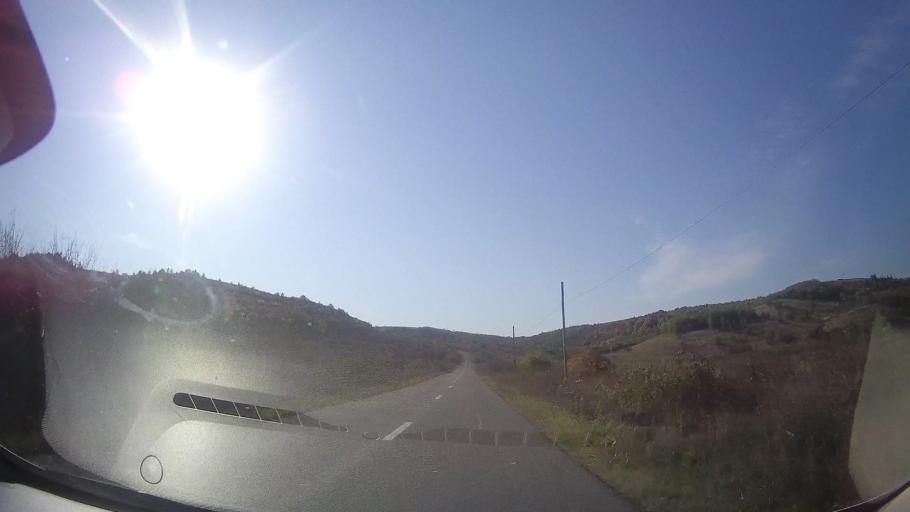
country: RO
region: Timis
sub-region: Oras Recas
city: Recas
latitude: 45.8449
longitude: 21.5199
